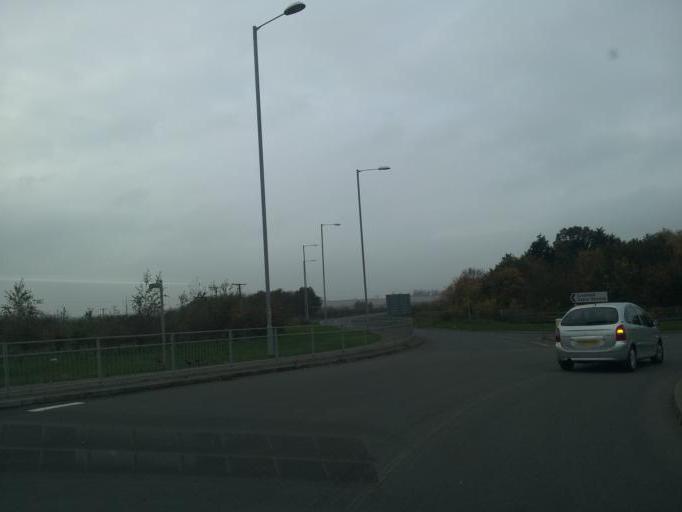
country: GB
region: England
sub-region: Central Bedfordshire
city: Marston Moretaine
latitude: 52.0668
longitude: -0.5549
